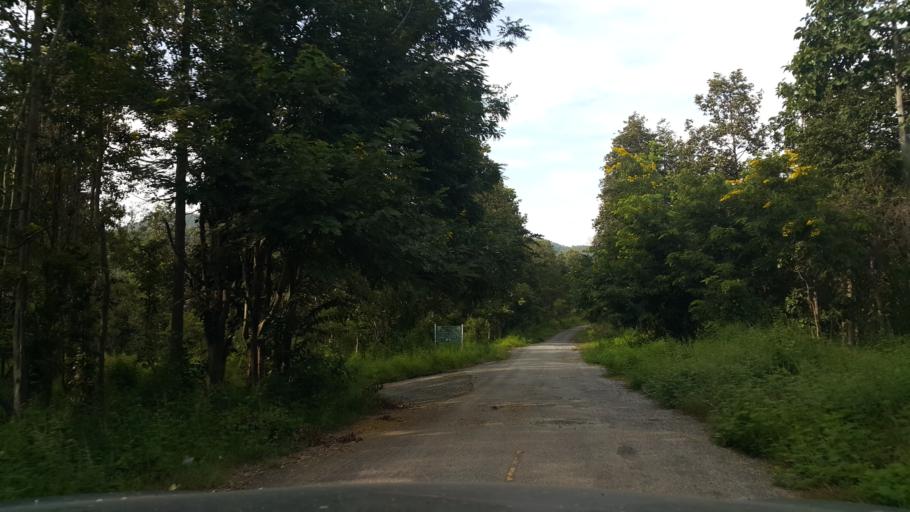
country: TH
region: Chiang Mai
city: San Sai
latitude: 18.9219
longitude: 99.0842
